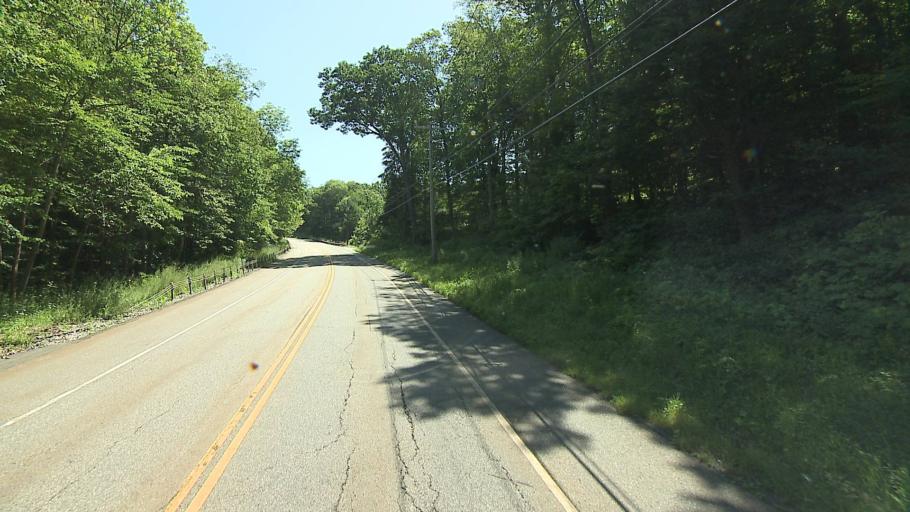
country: US
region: Connecticut
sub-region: Litchfield County
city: Litchfield
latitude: 41.8435
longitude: -73.3021
